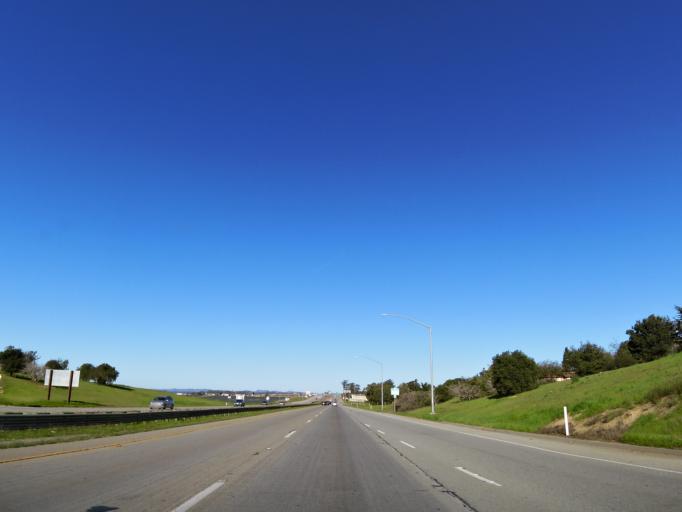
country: US
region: California
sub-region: Monterey County
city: Boronda
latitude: 36.7227
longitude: -121.6593
